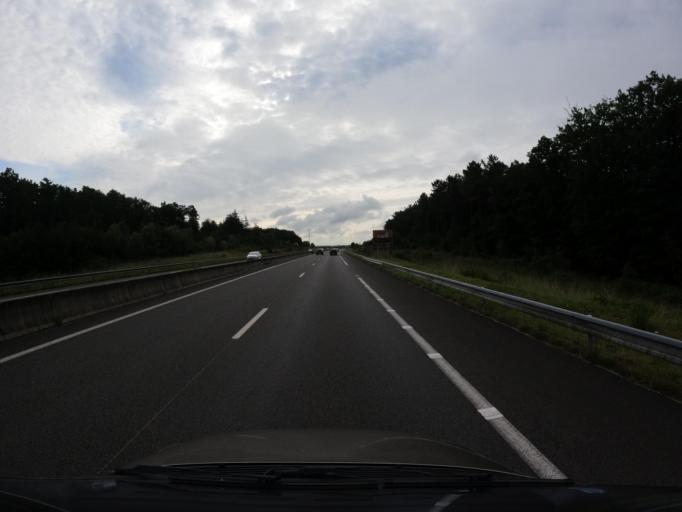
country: FR
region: Centre
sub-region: Departement d'Indre-et-Loire
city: Langeais
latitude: 47.3448
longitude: 0.4104
